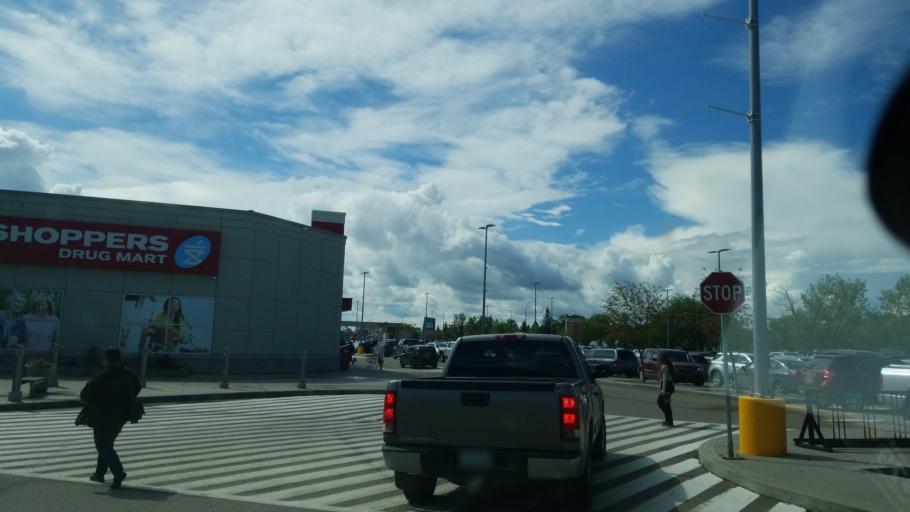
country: CA
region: Saskatchewan
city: Lloydminster
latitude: 53.2771
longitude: -110.0118
